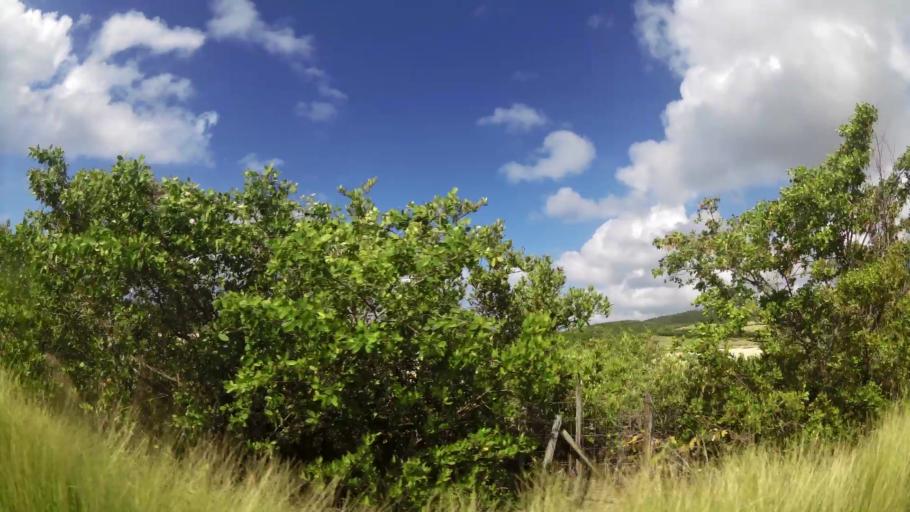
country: MQ
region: Martinique
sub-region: Martinique
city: Le Marin
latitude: 14.4058
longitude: -60.8758
